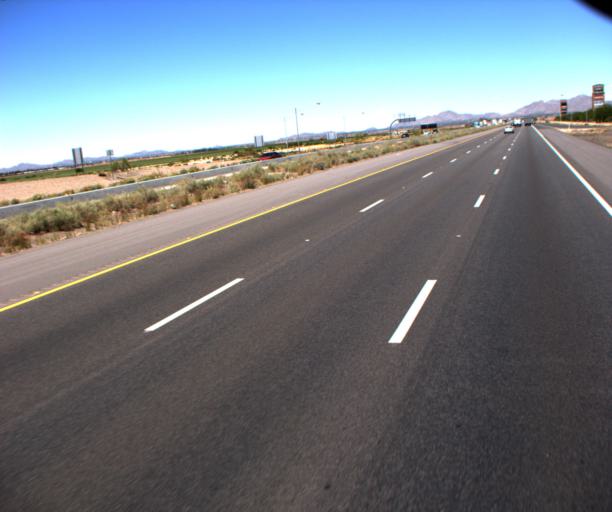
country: US
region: Arizona
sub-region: Pinal County
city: Casa Grande
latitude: 32.8806
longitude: -111.6867
